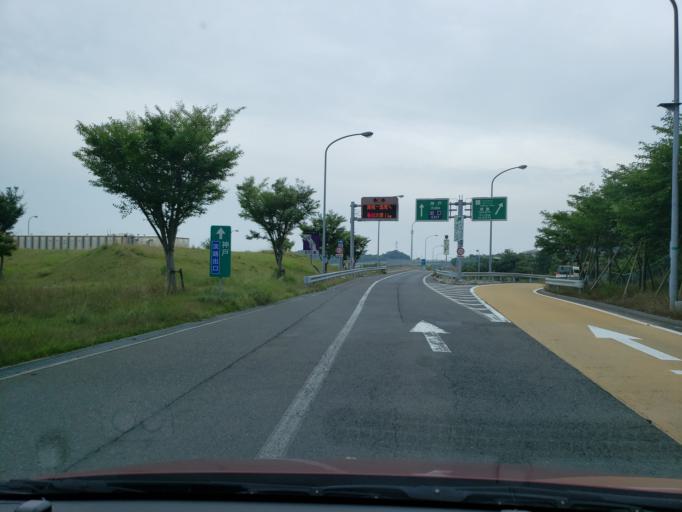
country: JP
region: Hyogo
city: Akashi
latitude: 34.5841
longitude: 135.0131
